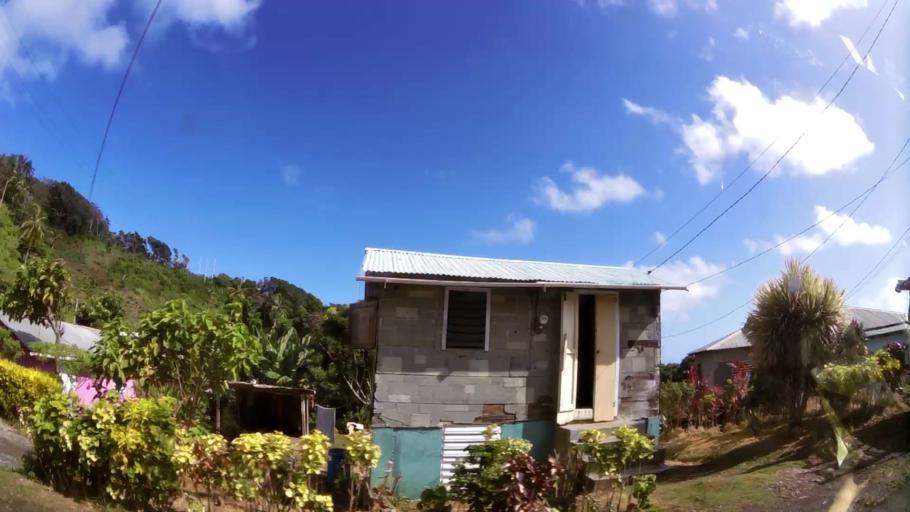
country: DM
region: Saint Andrew
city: Marigot
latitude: 15.5081
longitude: -61.2635
